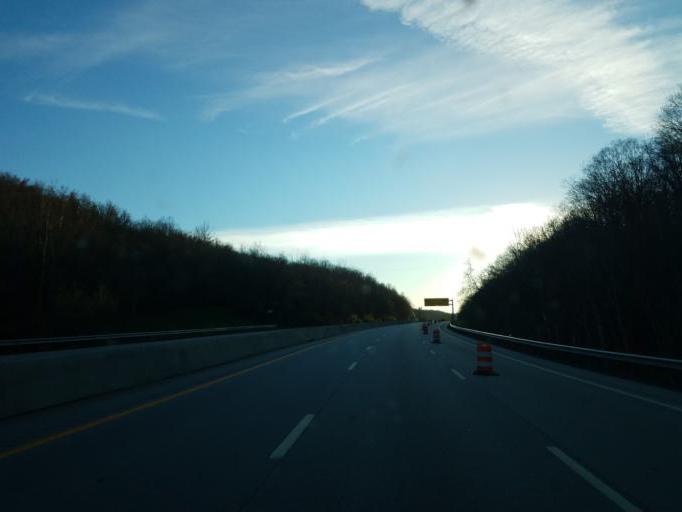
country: US
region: Ohio
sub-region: Belmont County
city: Wolfhurst
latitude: 40.0646
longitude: -80.7895
